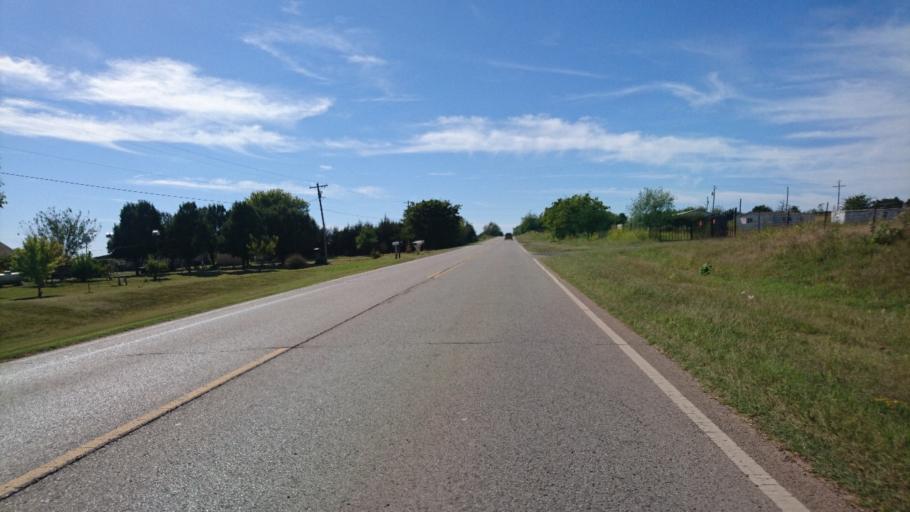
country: US
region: Oklahoma
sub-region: Lincoln County
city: Chandler
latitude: 35.7099
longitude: -96.7965
